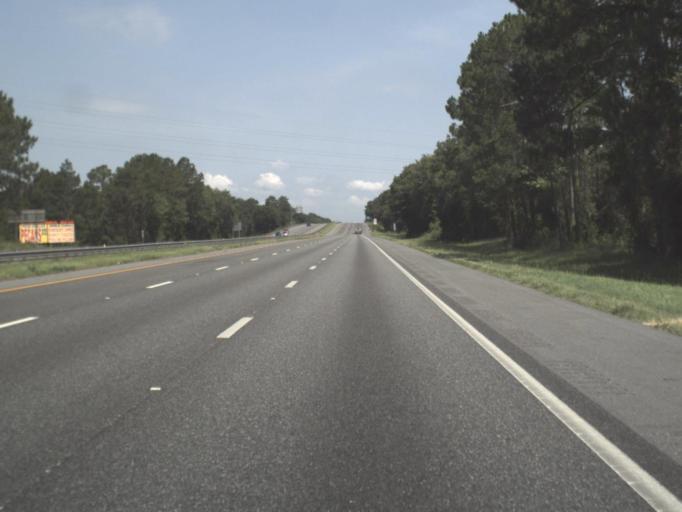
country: US
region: Florida
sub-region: Hamilton County
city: Jasper
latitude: 30.4532
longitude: -82.9401
